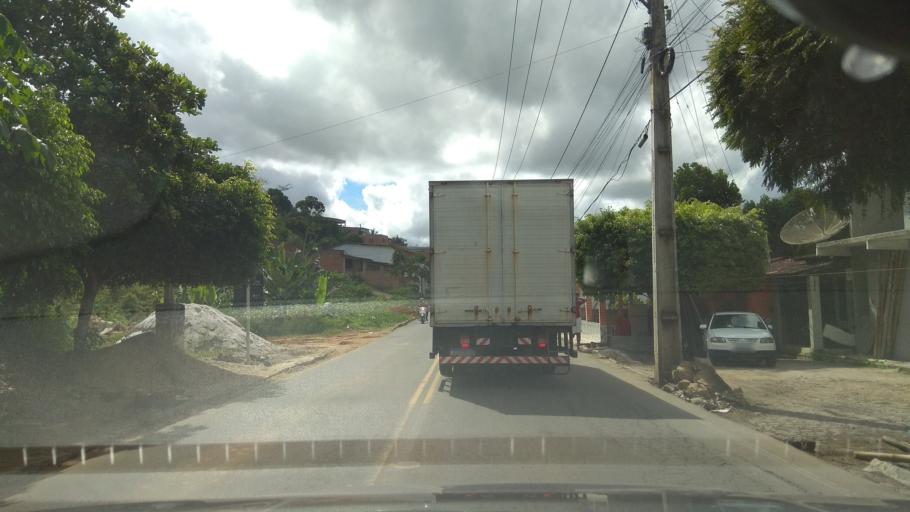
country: BR
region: Bahia
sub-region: Mutuipe
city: Mutuipe
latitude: -13.1783
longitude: -39.4131
